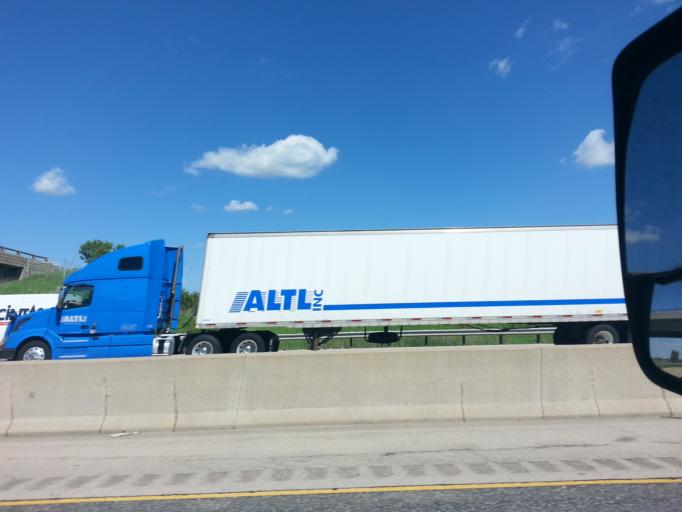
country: US
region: Illinois
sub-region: Winnebago County
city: Cherry Valley
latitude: 42.2897
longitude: -88.9649
